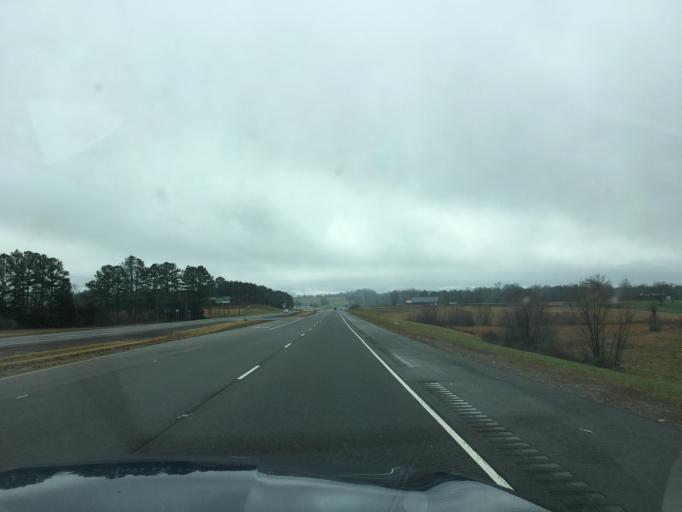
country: US
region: Tennessee
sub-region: McMinn County
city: Etowah
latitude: 35.3718
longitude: -84.5580
